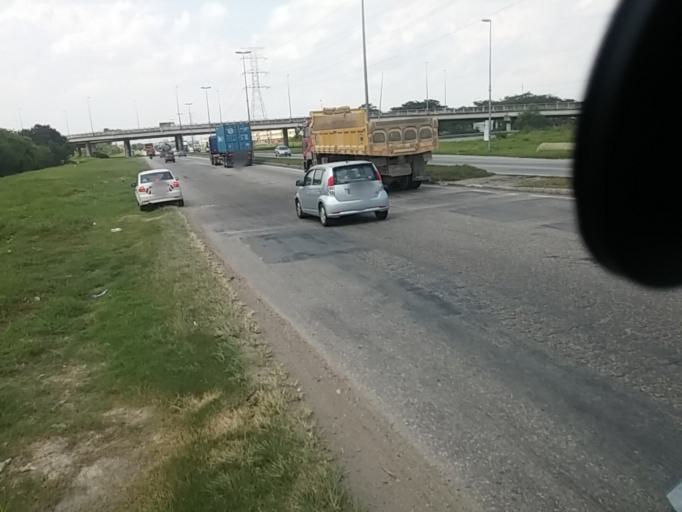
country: MY
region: Selangor
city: Klang
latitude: 2.9809
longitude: 101.4075
